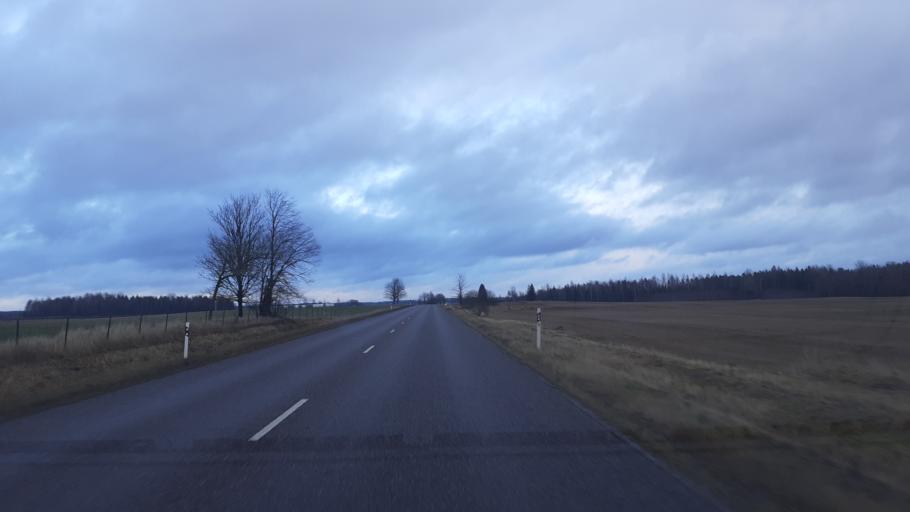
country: LV
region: Kuldigas Rajons
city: Kuldiga
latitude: 57.0132
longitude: 22.1575
